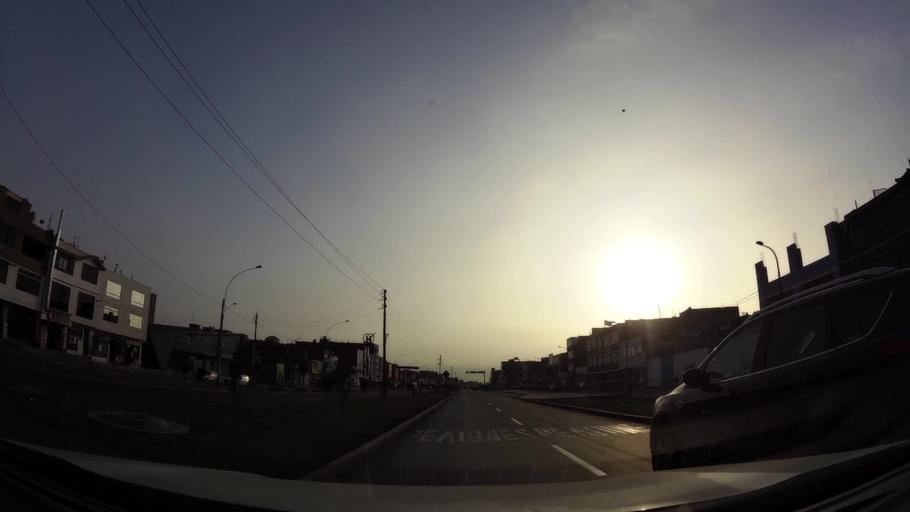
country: PE
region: Lima
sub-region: Lima
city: Independencia
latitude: -11.9910
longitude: -77.0874
